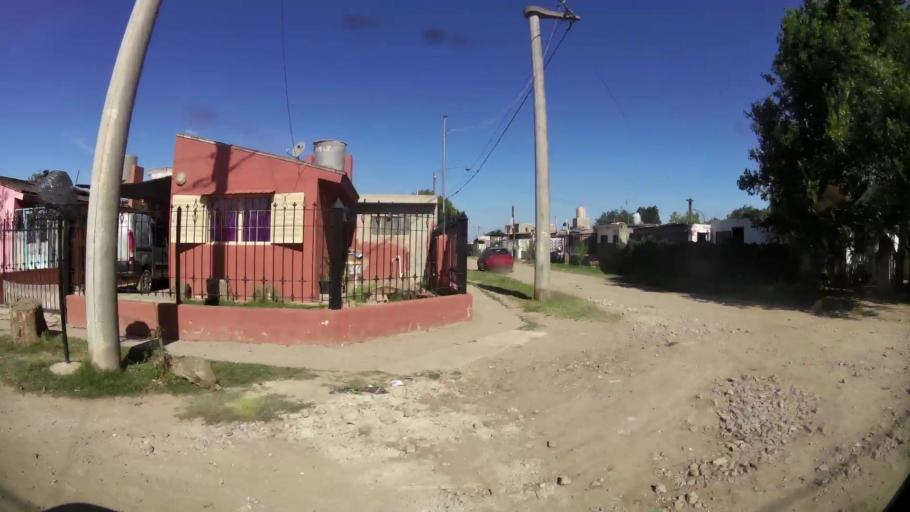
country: AR
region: Cordoba
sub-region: Departamento de Capital
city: Cordoba
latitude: -31.3737
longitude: -64.1906
